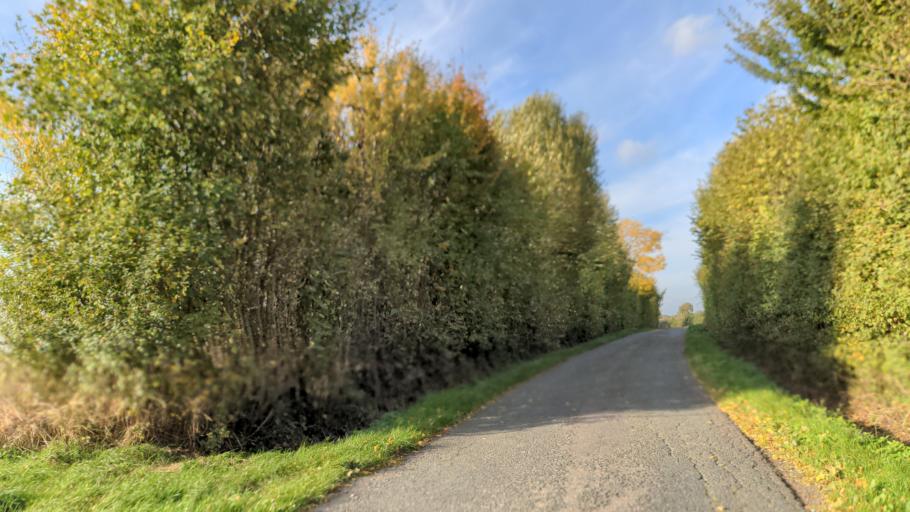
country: DE
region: Schleswig-Holstein
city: Monkhagen
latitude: 53.9290
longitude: 10.5748
